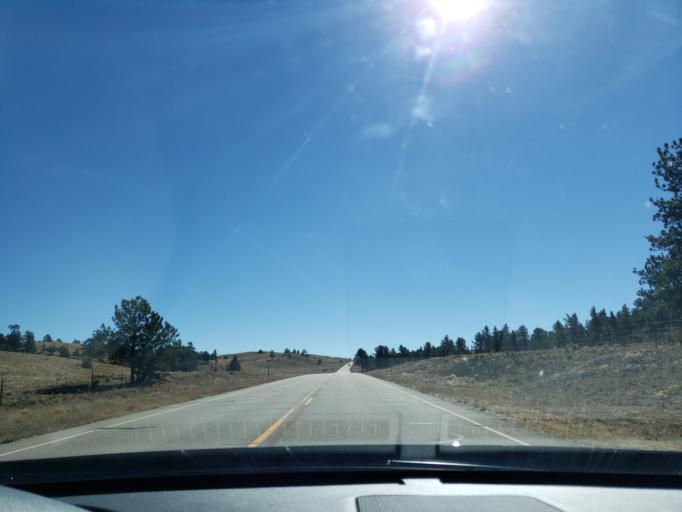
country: US
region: Colorado
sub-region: Park County
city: Fairplay
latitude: 38.9176
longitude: -105.7065
